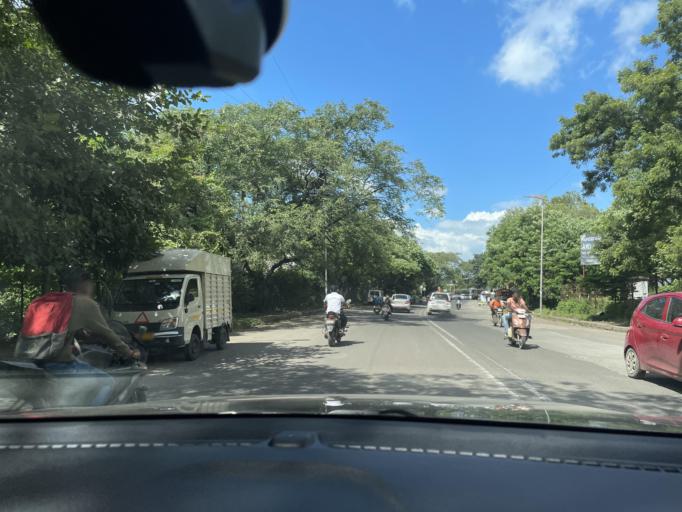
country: IN
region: Maharashtra
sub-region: Pune Division
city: Shivaji Nagar
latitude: 18.5241
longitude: 73.7805
